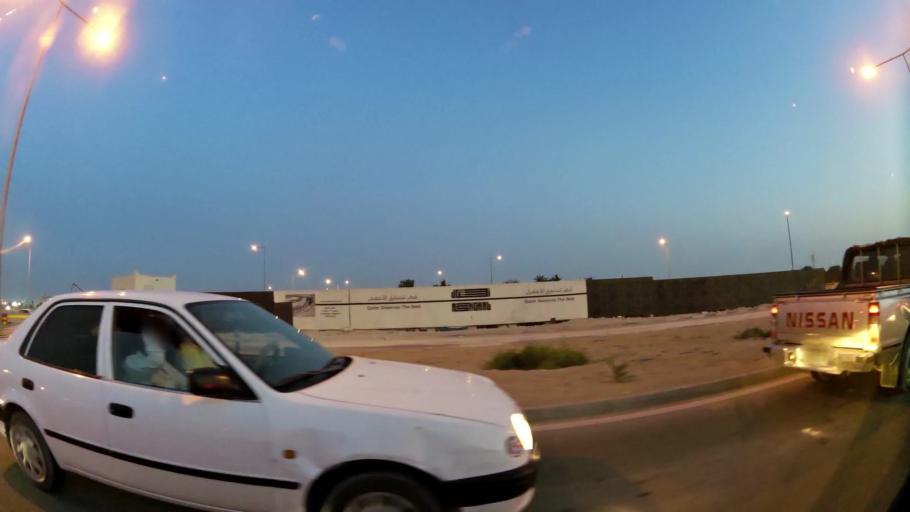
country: QA
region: Baladiyat ar Rayyan
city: Ar Rayyan
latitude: 25.3016
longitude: 51.4499
